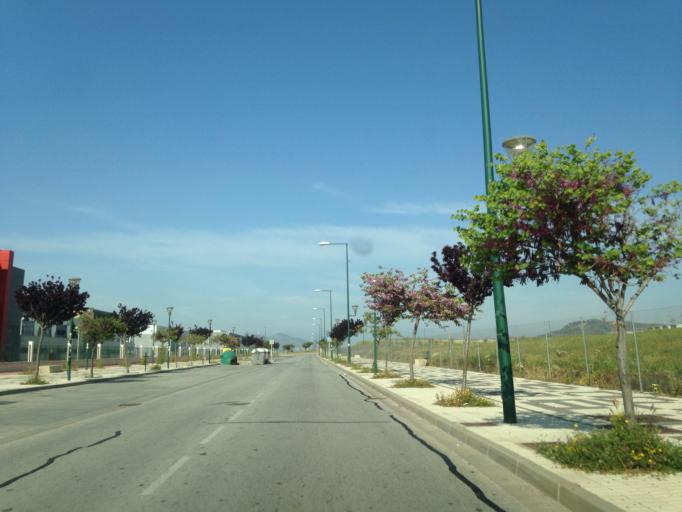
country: ES
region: Andalusia
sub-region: Provincia de Malaga
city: Malaga
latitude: 36.7162
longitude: -4.4917
